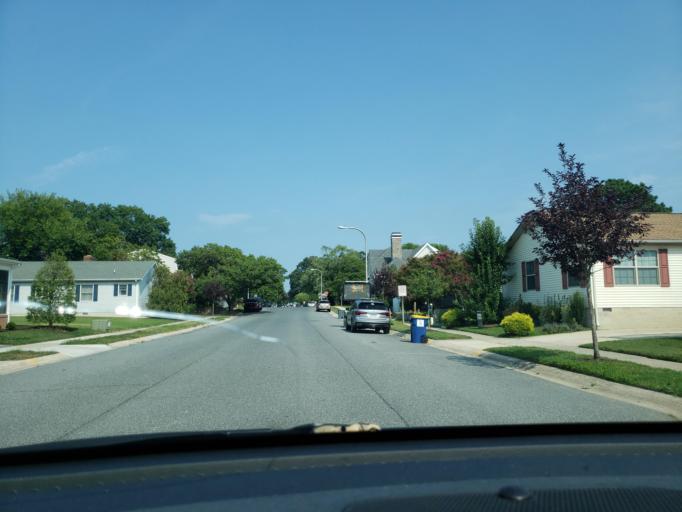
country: US
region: Delaware
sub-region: Sussex County
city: Rehoboth Beach
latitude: 38.7133
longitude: -75.0868
